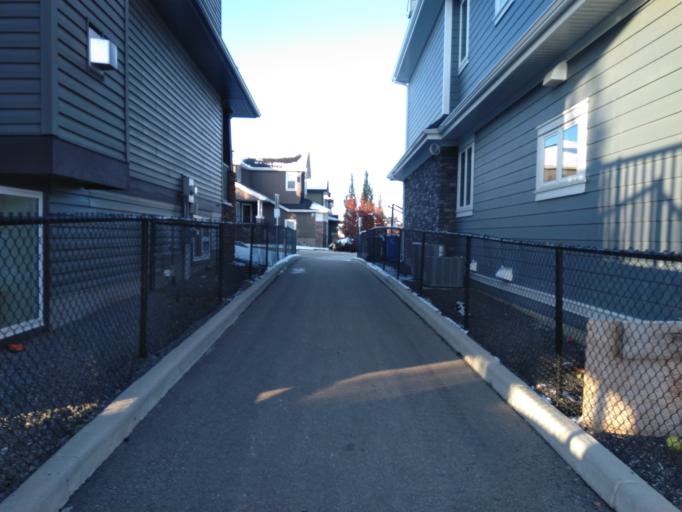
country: CA
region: Alberta
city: Cochrane
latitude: 51.1812
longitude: -114.5043
